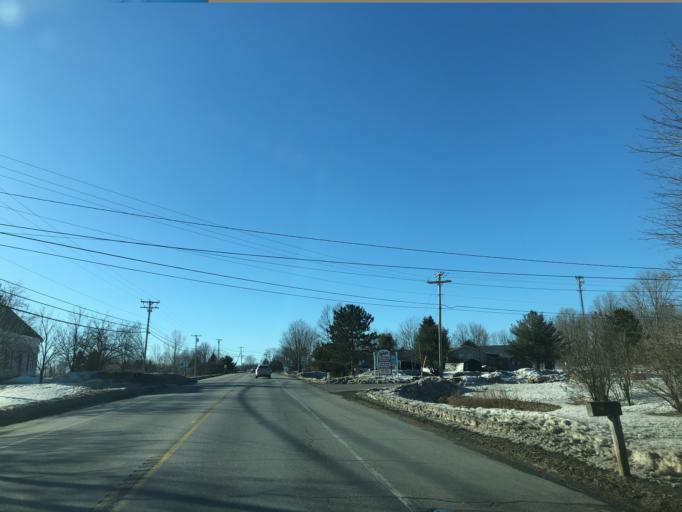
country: US
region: Maine
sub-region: Penobscot County
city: Charleston
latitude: 44.9880
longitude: -69.0118
